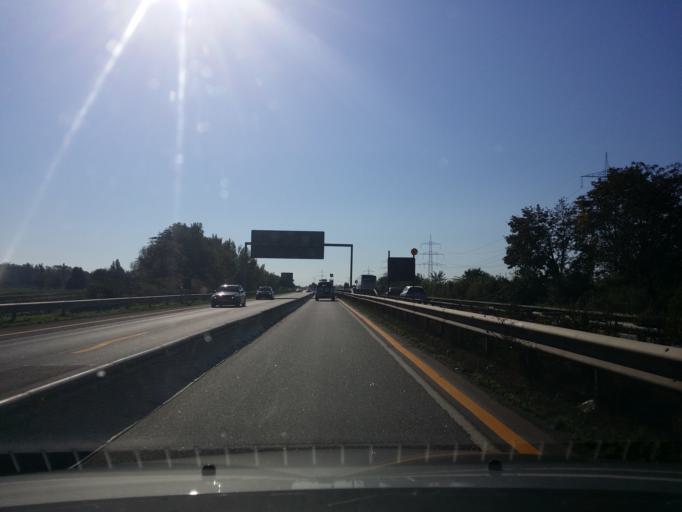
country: DE
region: Rheinland-Pfalz
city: Fussgonheim
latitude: 49.4673
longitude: 8.3133
